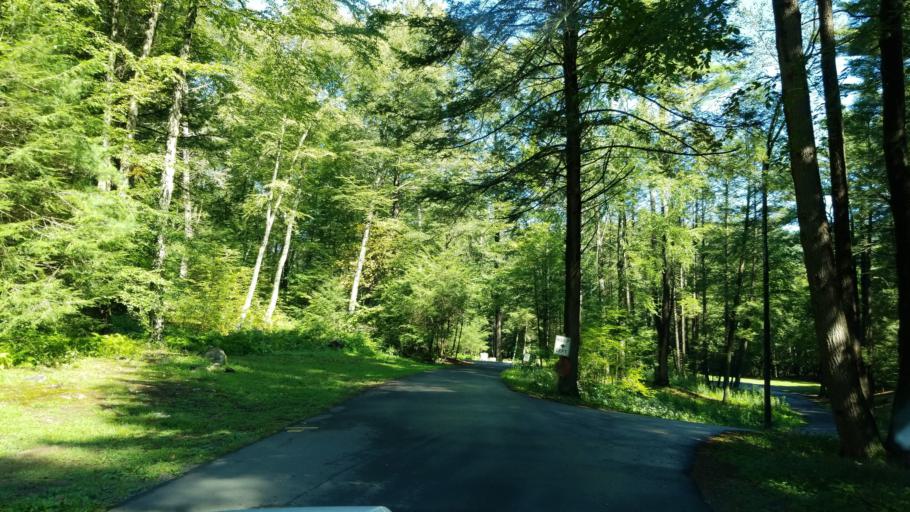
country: US
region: Connecticut
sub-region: Litchfield County
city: Thomaston
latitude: 41.6549
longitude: -73.1012
